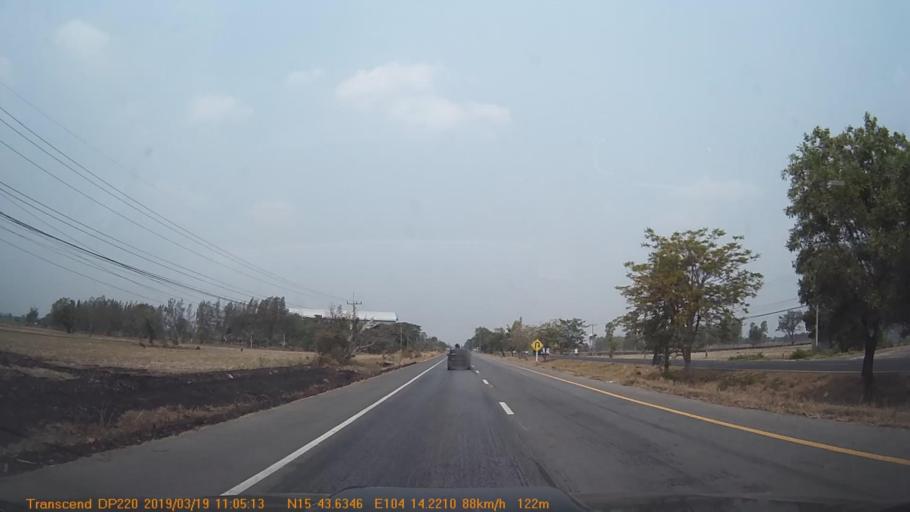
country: TH
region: Yasothon
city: Kham Khuean Kaeo
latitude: 15.7274
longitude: 104.2369
